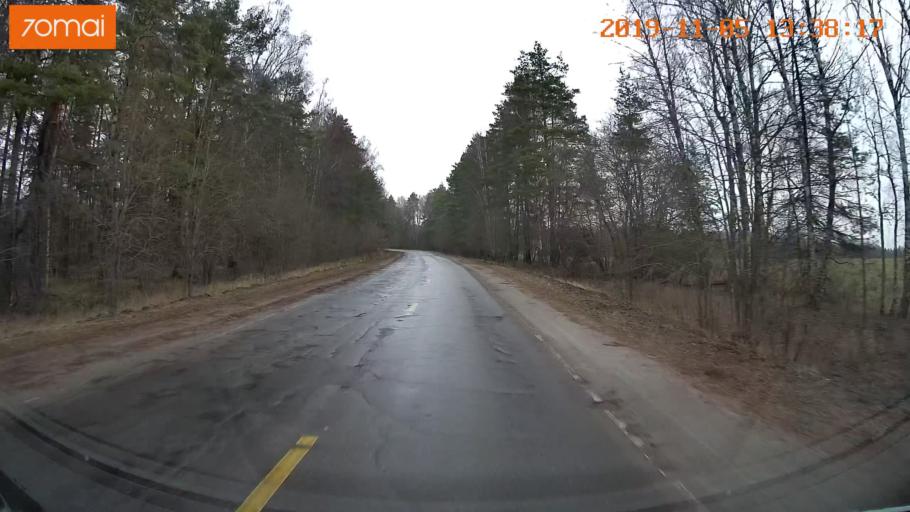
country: RU
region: Ivanovo
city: Shuya
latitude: 56.9305
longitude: 41.3858
